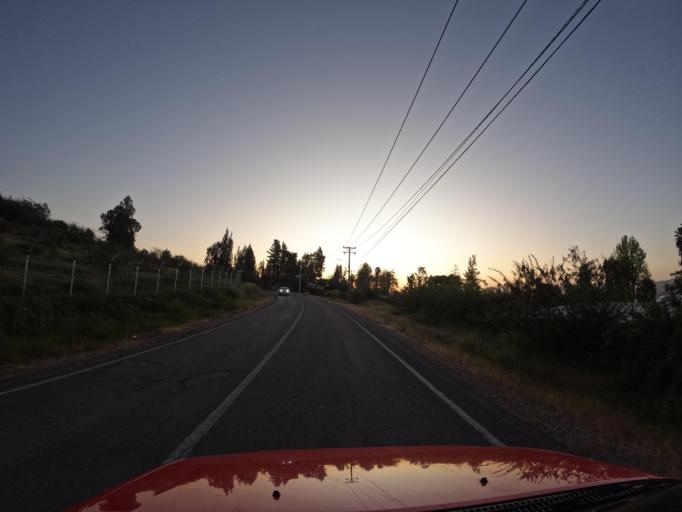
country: CL
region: O'Higgins
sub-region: Provincia de Cachapoal
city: San Vicente
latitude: -34.1556
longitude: -71.4224
